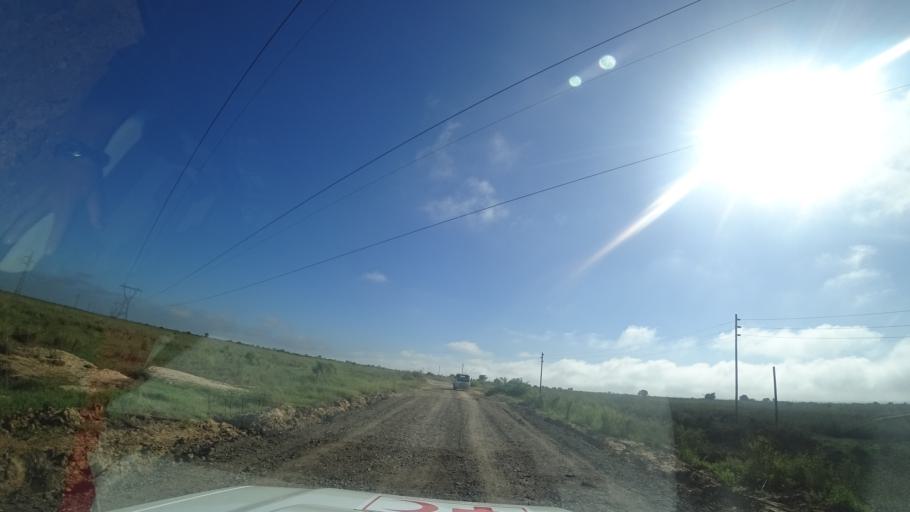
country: MZ
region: Sofala
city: Dondo
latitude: -19.4596
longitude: 34.5631
